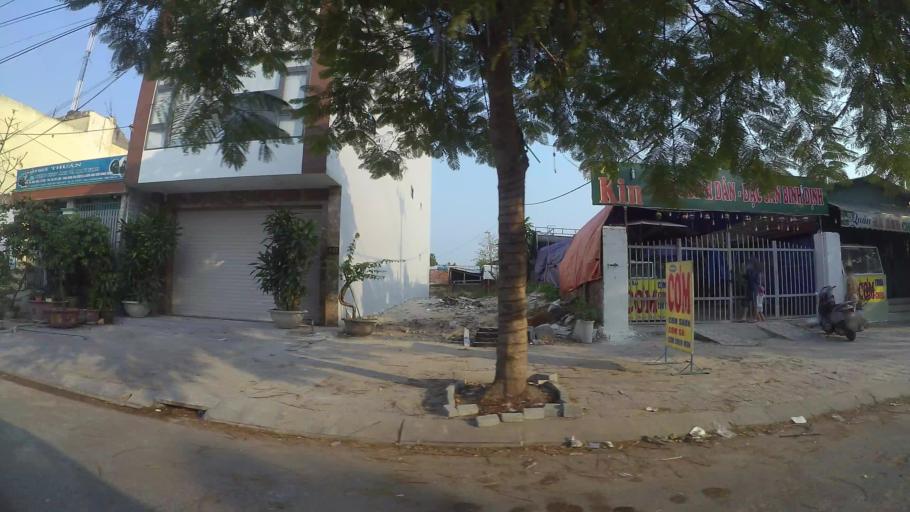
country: VN
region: Da Nang
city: Ngu Hanh Son
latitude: 15.9853
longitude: 108.2402
